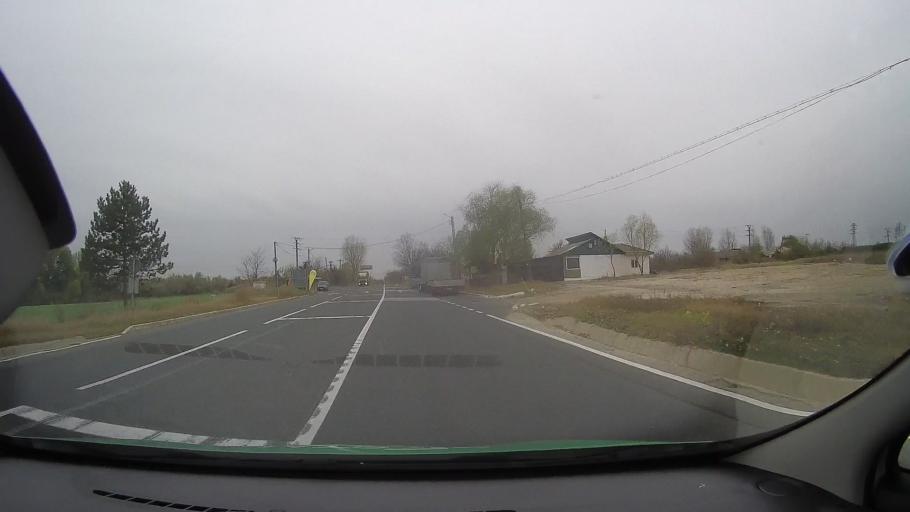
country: RO
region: Constanta
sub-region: Oras Harsova
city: Harsova
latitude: 44.6915
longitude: 27.9659
